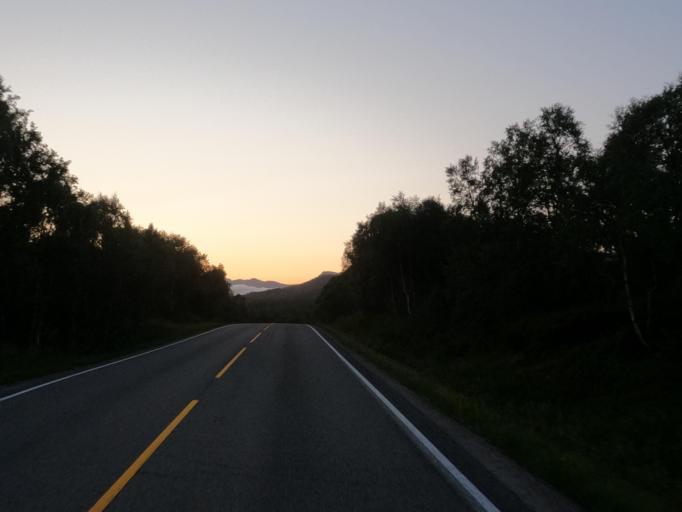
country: NO
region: Nordland
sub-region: Lodingen
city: Lodingen
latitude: 68.5133
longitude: 15.8774
